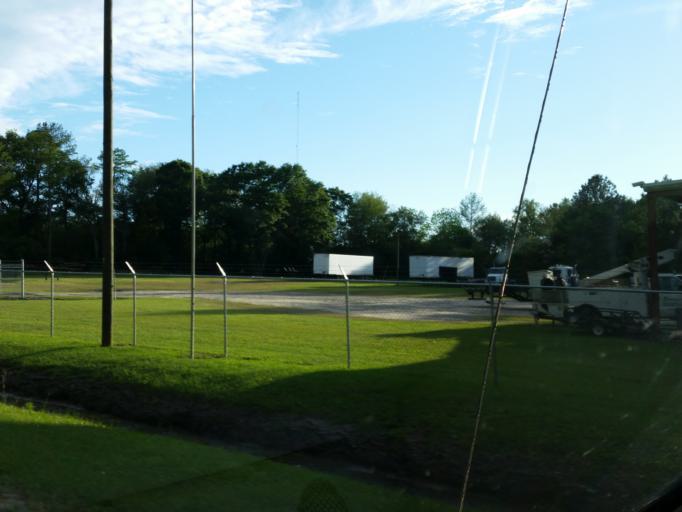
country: US
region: Georgia
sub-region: Turner County
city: Ashburn
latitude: 31.6903
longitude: -83.6407
